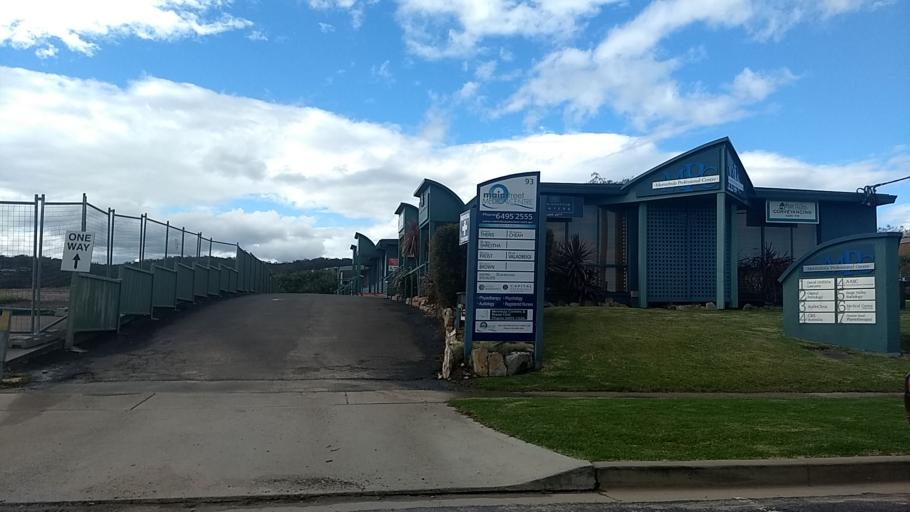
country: AU
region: New South Wales
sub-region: Bega Valley
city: Merimbula
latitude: -36.8868
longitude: 149.9112
